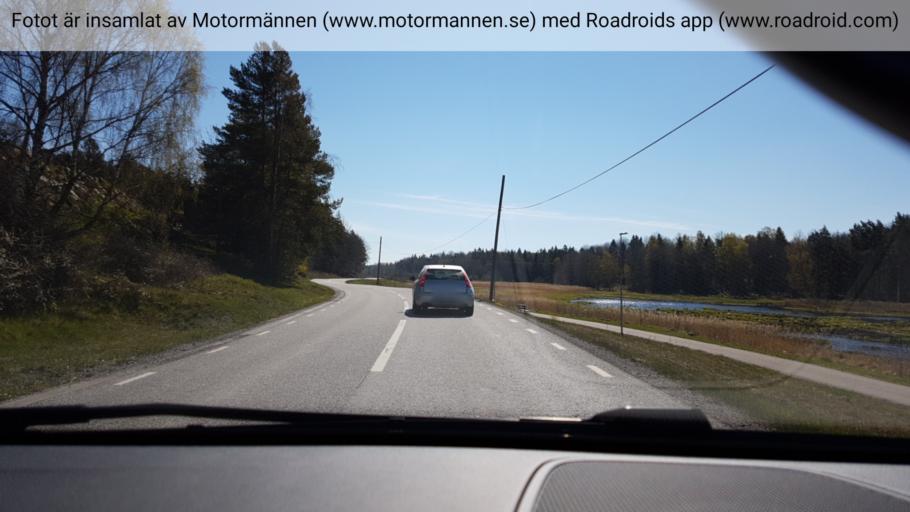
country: SE
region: Stockholm
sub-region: Varmdo Kommun
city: Hemmesta
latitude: 59.3268
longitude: 18.5119
